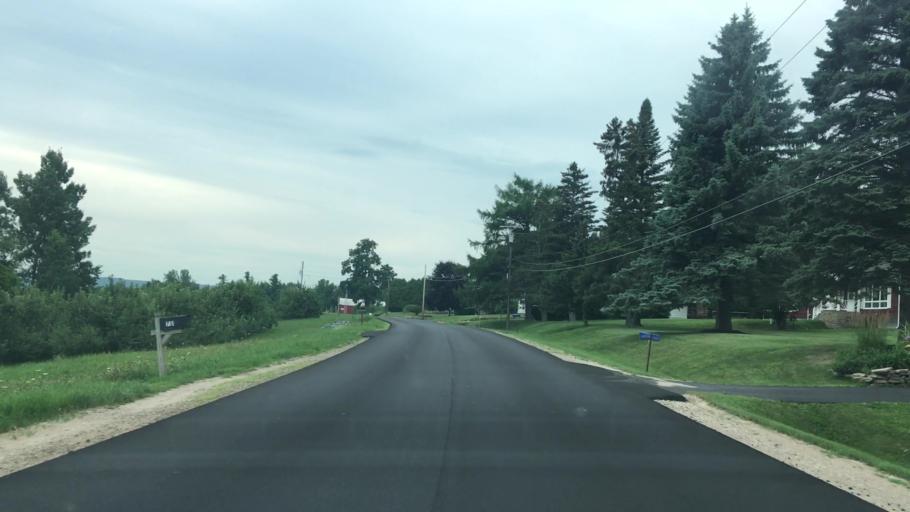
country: US
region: New York
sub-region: Clinton County
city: Peru
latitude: 44.5697
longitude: -73.5709
